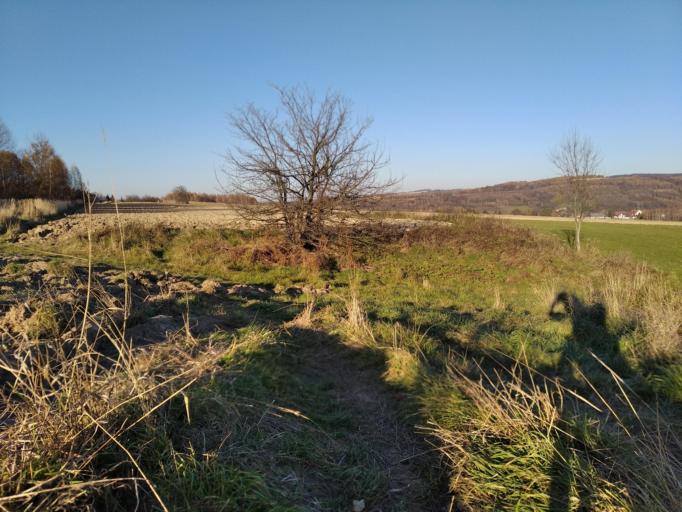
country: PL
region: Subcarpathian Voivodeship
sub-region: Powiat strzyzowski
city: Strzyzow
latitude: 49.8393
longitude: 21.7978
